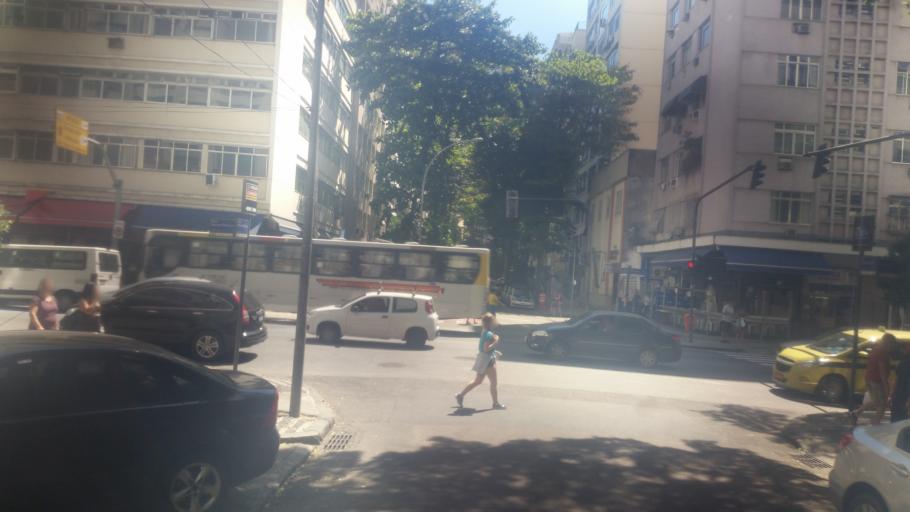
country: BR
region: Rio de Janeiro
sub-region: Rio De Janeiro
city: Rio de Janeiro
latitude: -22.9678
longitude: -43.1844
